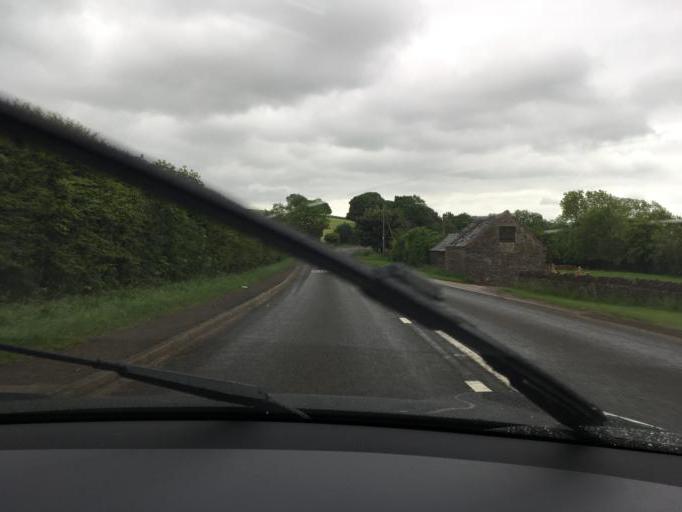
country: GB
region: England
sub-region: Staffordshire
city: Mayfield
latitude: 53.0324
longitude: -1.8051
